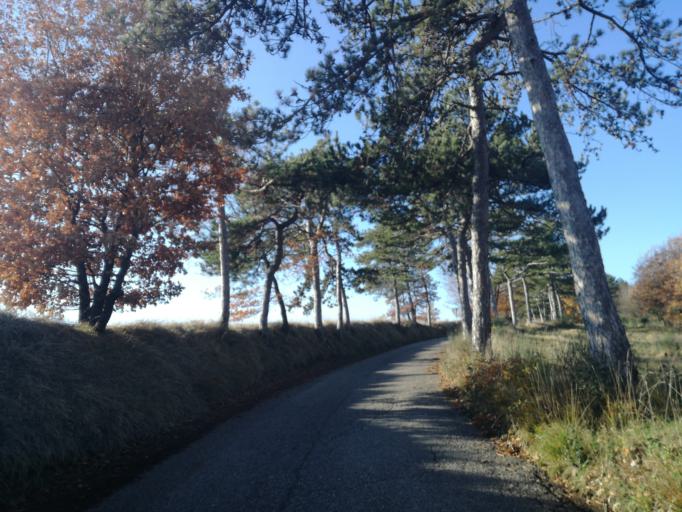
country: IT
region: Umbria
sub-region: Provincia di Perugia
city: Perugia
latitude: 43.0748
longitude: 12.3814
